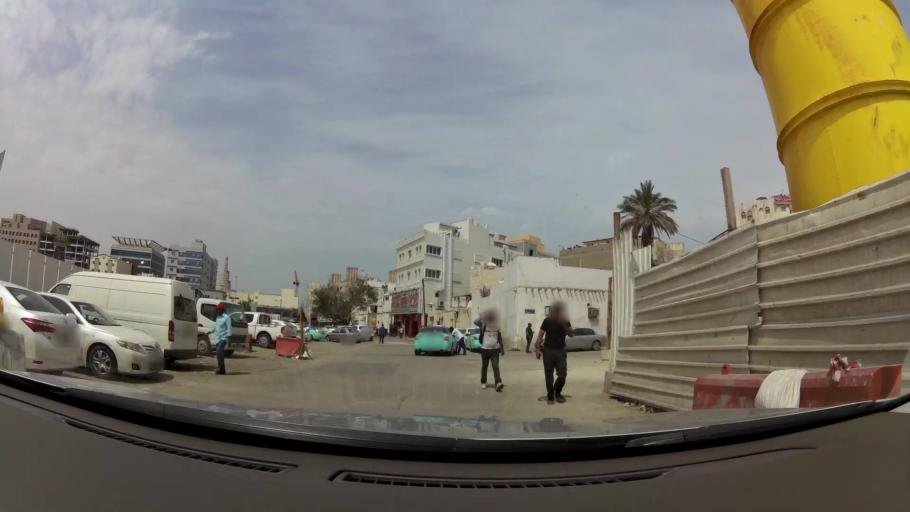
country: QA
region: Baladiyat ad Dawhah
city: Doha
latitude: 25.2840
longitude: 51.5370
